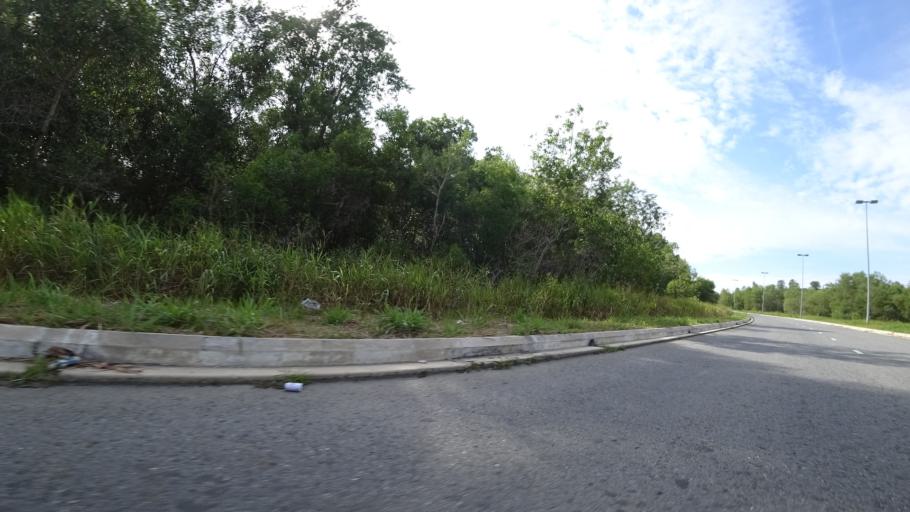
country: BN
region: Brunei and Muara
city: Bandar Seri Begawan
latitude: 4.8987
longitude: 114.8028
